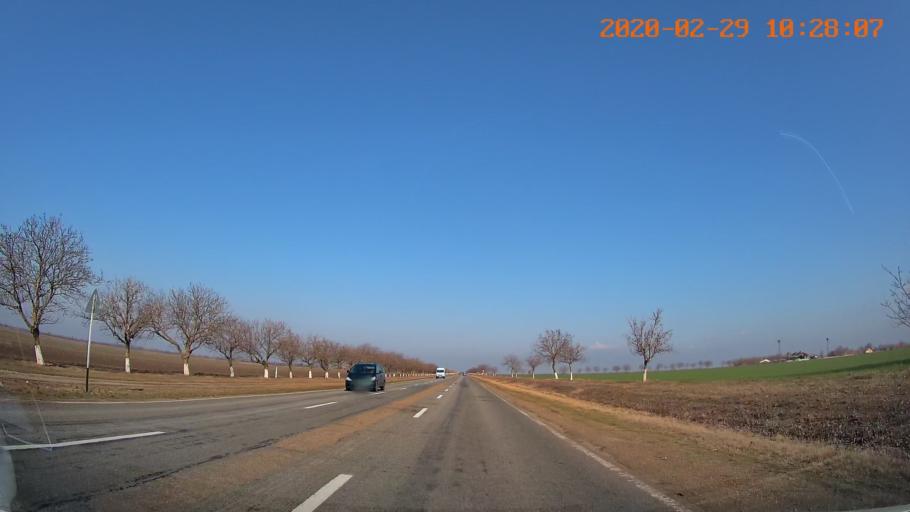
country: MD
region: Telenesti
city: Tiraspolul Nou
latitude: 46.9059
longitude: 29.5934
